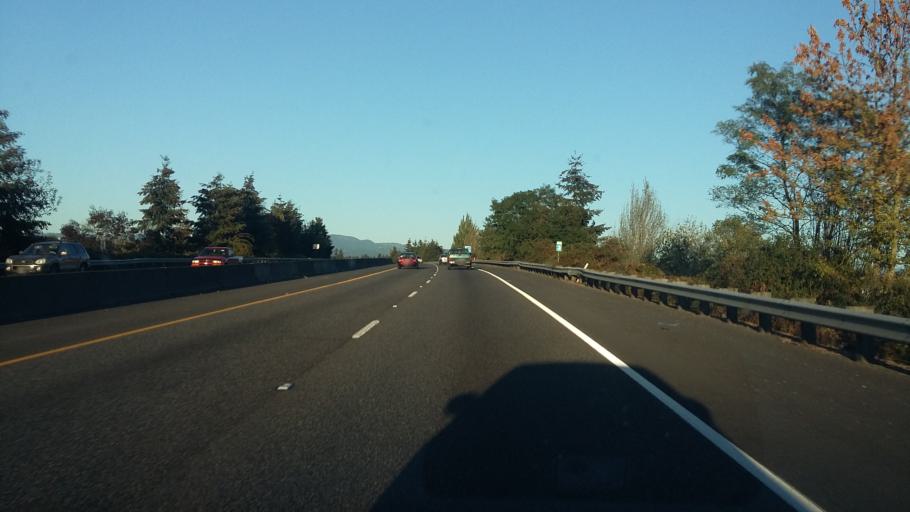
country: US
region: Washington
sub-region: Clark County
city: Walnut Grove
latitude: 45.6480
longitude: -122.6049
